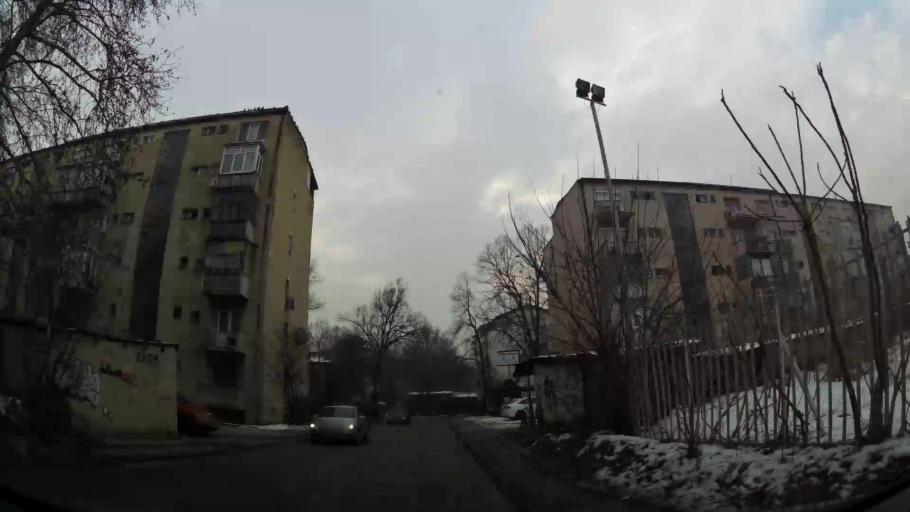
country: MK
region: Cair
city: Cair
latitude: 42.0058
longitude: 21.4655
